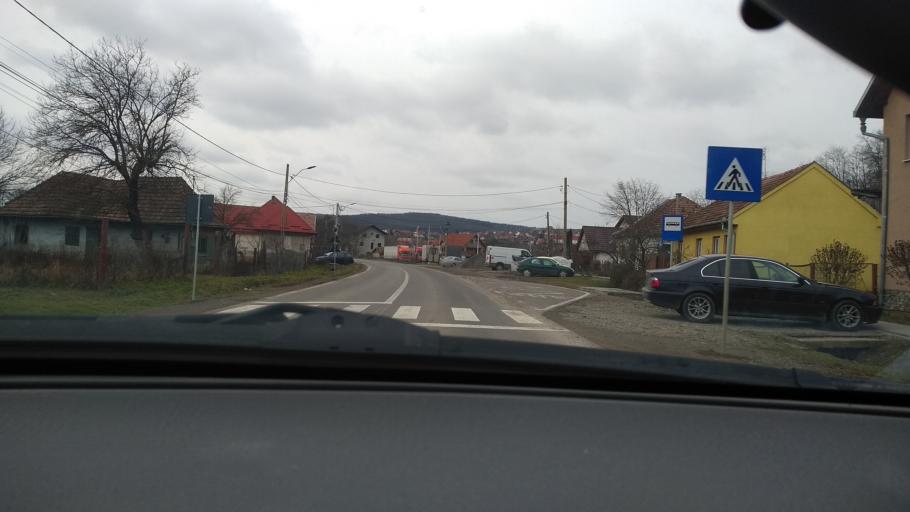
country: RO
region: Mures
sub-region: Comuna Livezeni
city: Livezeni
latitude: 46.5468
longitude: 24.6379
